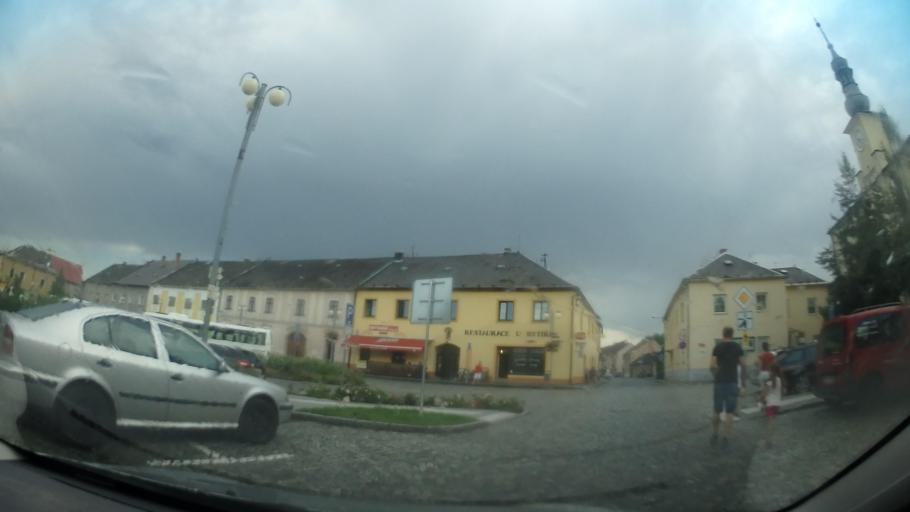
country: CZ
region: Olomoucky
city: Lostice
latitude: 49.7452
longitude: 16.9279
